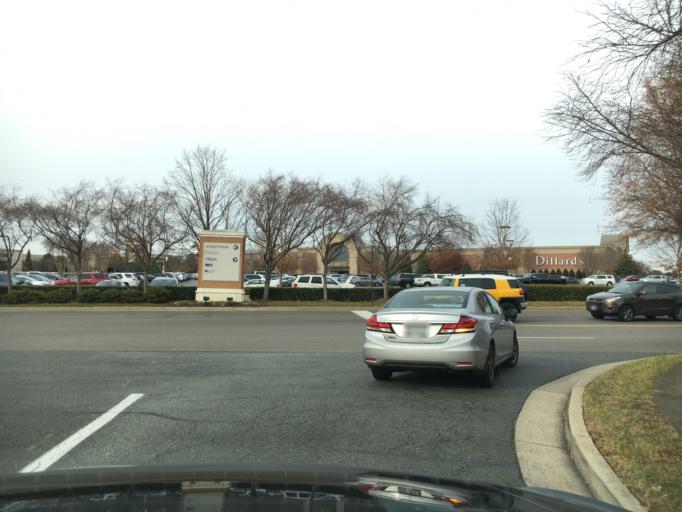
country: US
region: Virginia
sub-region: Henrico County
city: Short Pump
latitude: 37.6537
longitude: -77.6160
